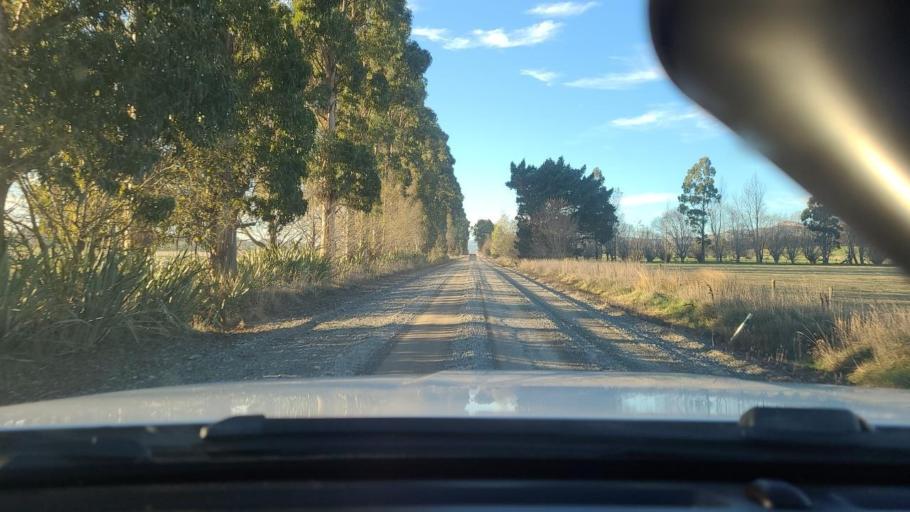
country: NZ
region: Southland
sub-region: Southland District
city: Winton
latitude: -45.8876
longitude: 168.5248
